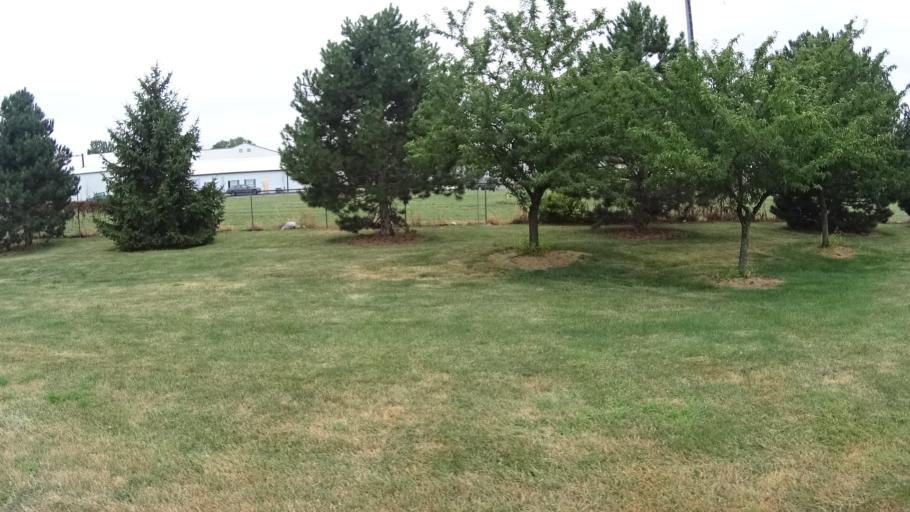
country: US
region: Ohio
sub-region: Erie County
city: Sandusky
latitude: 41.4386
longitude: -82.6693
